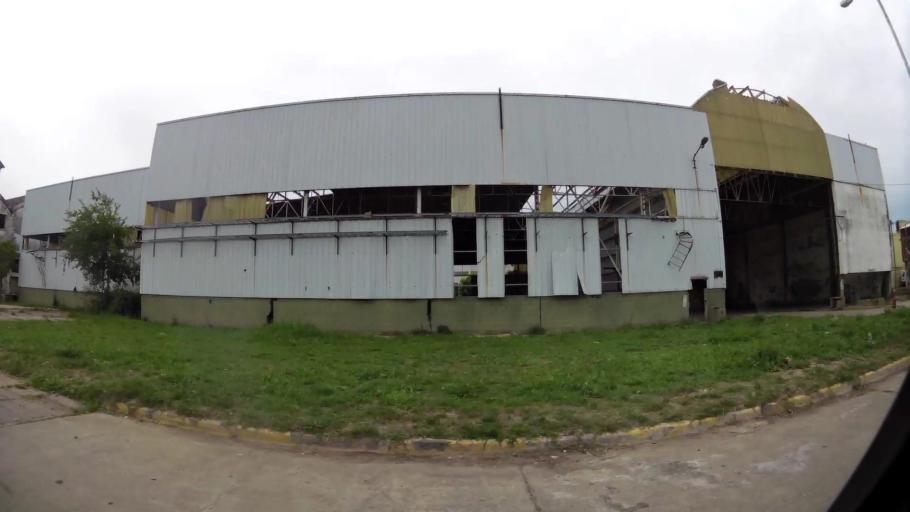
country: AR
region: Buenos Aires
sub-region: Partido de Avellaneda
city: Avellaneda
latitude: -34.6496
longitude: -58.3582
